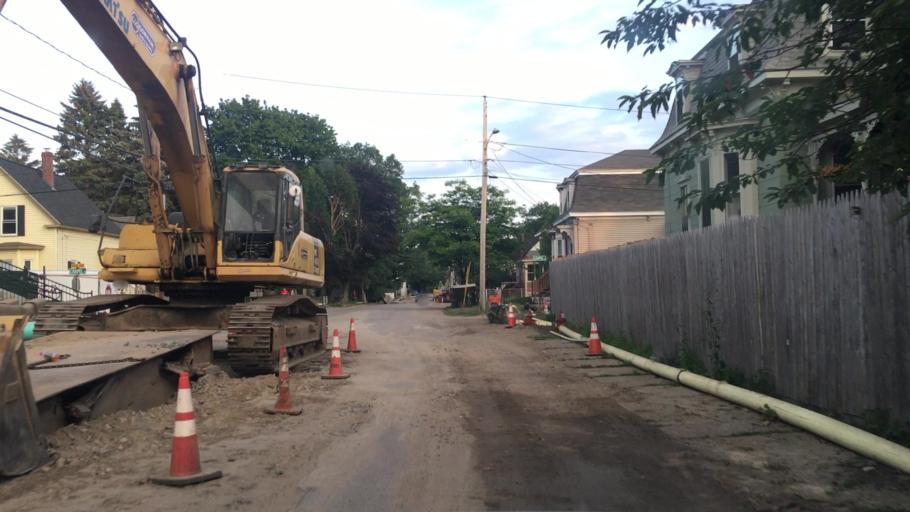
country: US
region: Maine
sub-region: Cumberland County
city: South Portland
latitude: 43.6332
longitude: -70.2685
